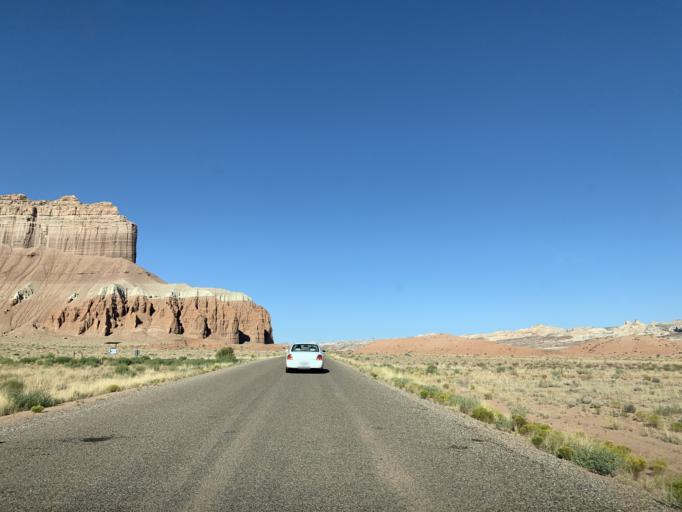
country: US
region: Utah
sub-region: Emery County
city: Ferron
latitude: 38.5824
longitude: -110.7103
